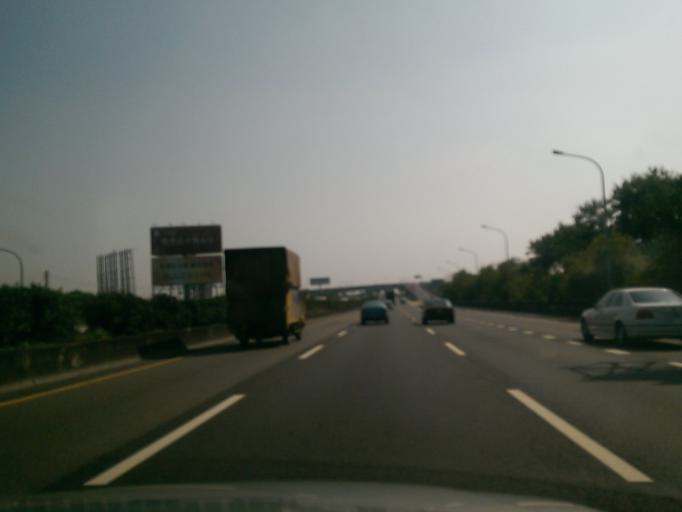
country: TW
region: Taiwan
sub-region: Taichung City
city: Taichung
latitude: 24.1251
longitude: 120.6198
